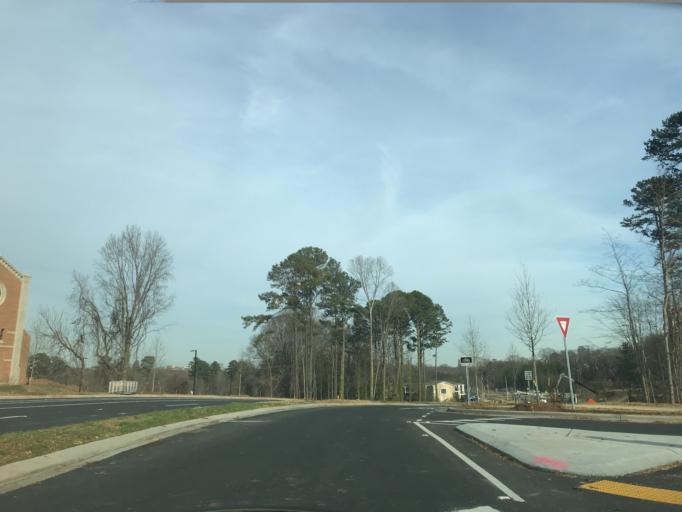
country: US
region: North Carolina
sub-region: Wake County
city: West Raleigh
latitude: 35.7762
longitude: -78.6705
